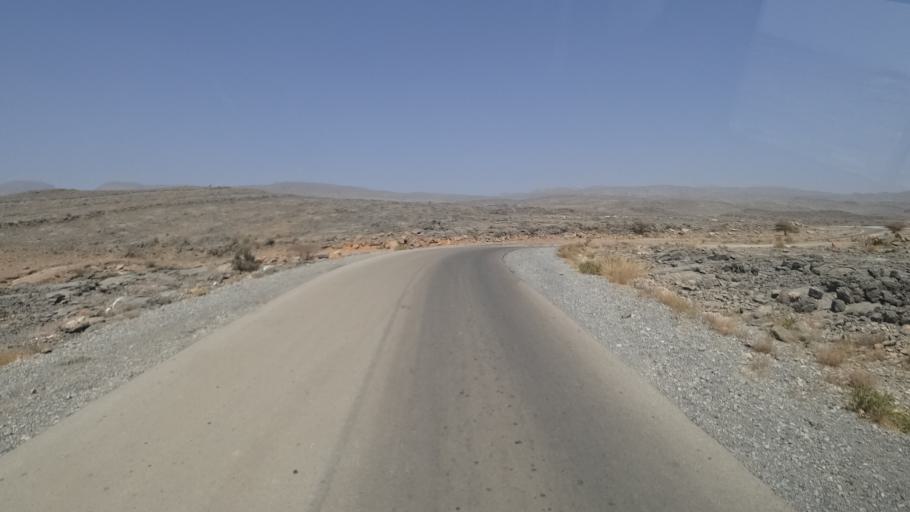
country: OM
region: Muhafazat ad Dakhiliyah
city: Bahla'
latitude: 23.1037
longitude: 57.3542
